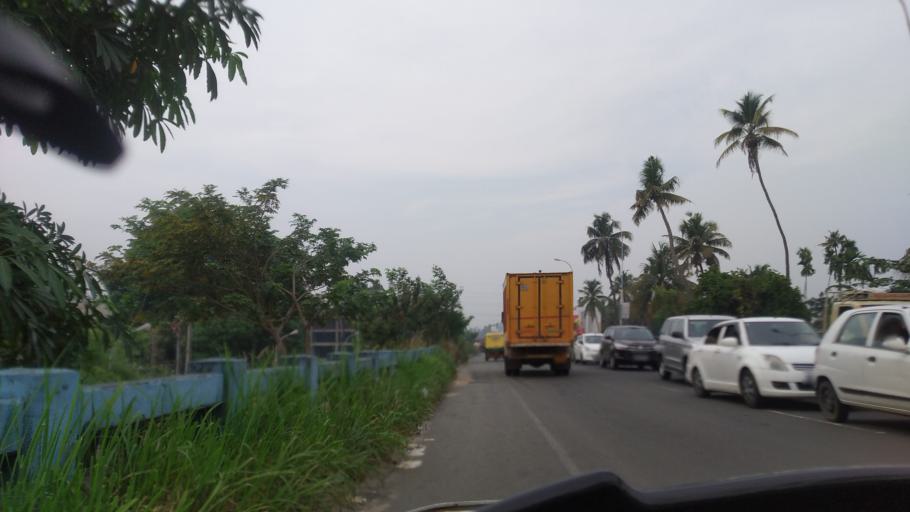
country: IN
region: Kerala
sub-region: Ernakulam
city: Elur
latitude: 10.0389
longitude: 76.3012
